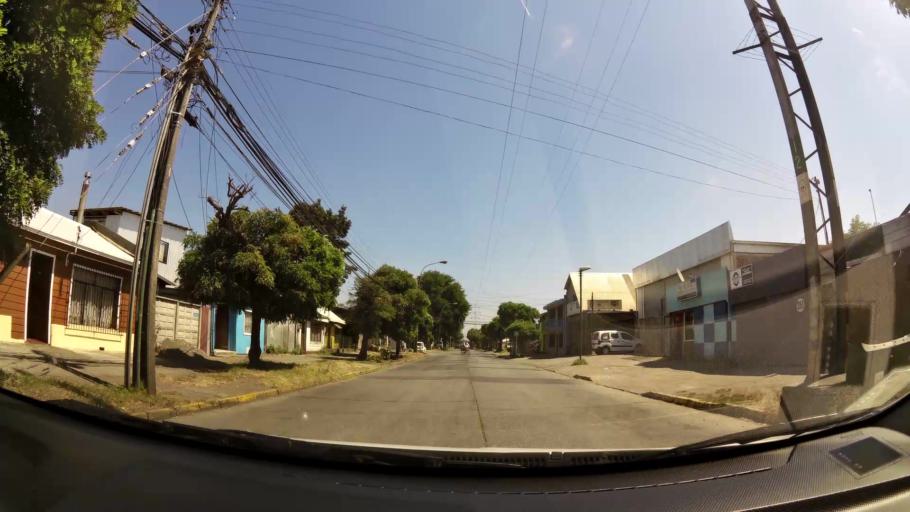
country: CL
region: Biobio
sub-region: Provincia de Concepcion
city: Concepcion
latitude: -36.8089
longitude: -73.0519
